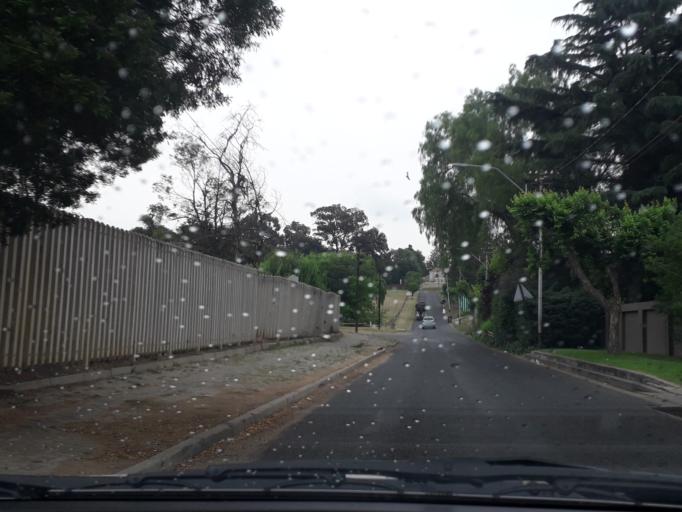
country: ZA
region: Gauteng
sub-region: City of Johannesburg Metropolitan Municipality
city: Modderfontein
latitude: -26.1330
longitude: 28.1038
